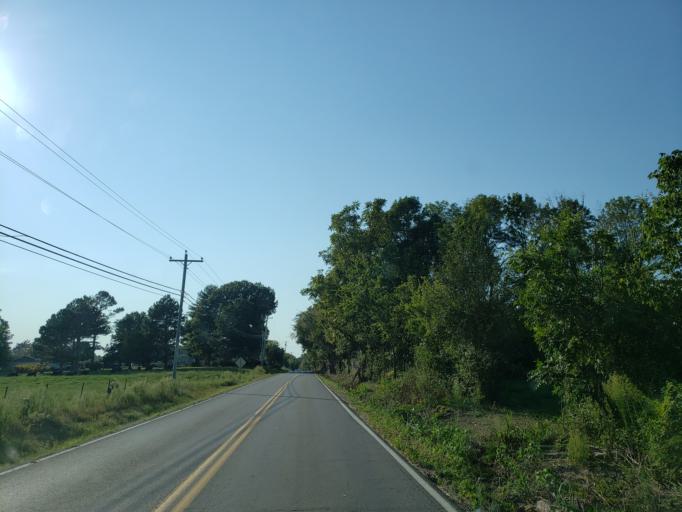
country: US
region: Tennessee
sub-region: Bradley County
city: Wildwood Lake
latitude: 35.1023
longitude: -84.8103
